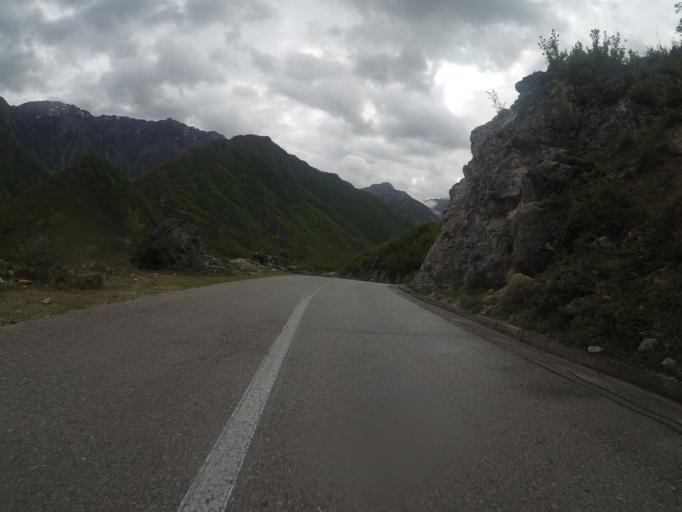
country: BA
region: Federation of Bosnia and Herzegovina
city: Siroki Brijeg
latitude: 43.5393
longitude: 17.6200
